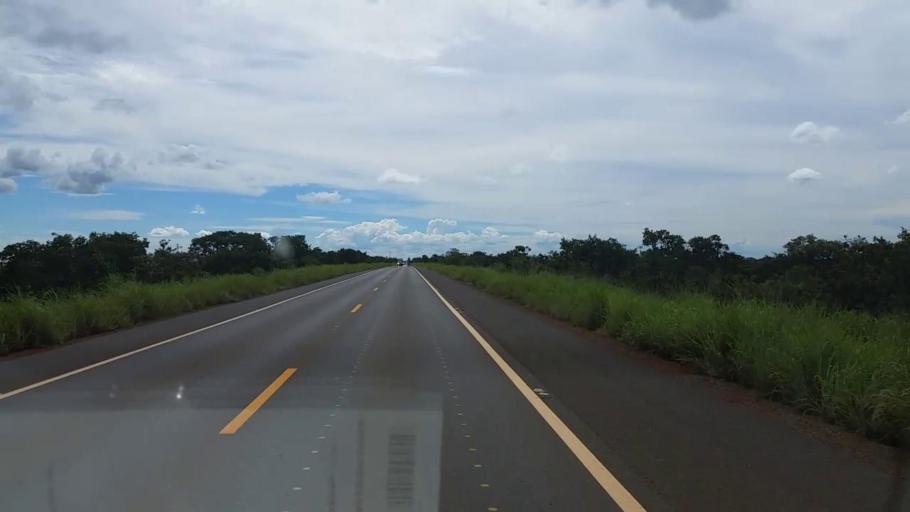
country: BR
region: Goias
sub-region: Luziania
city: Luziania
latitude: -16.2090
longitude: -47.4216
